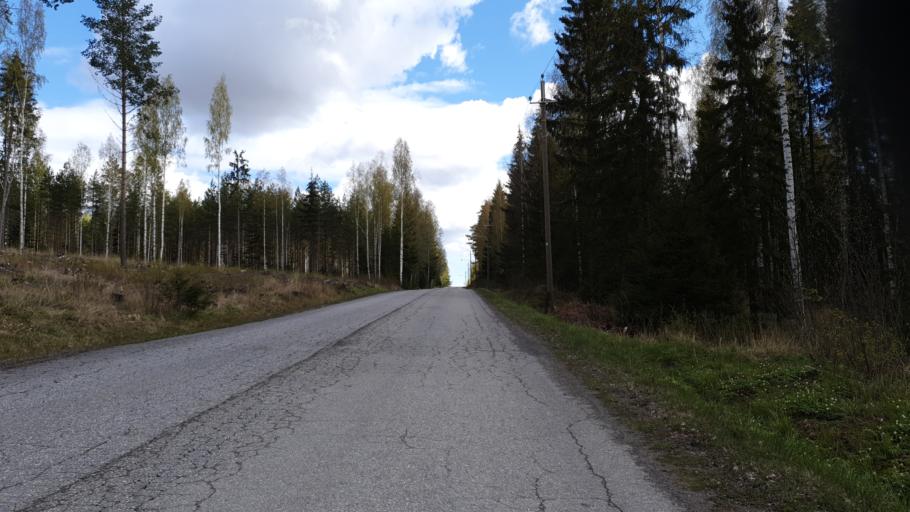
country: FI
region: Uusimaa
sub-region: Helsinki
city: Nurmijaervi
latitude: 60.3838
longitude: 24.8938
